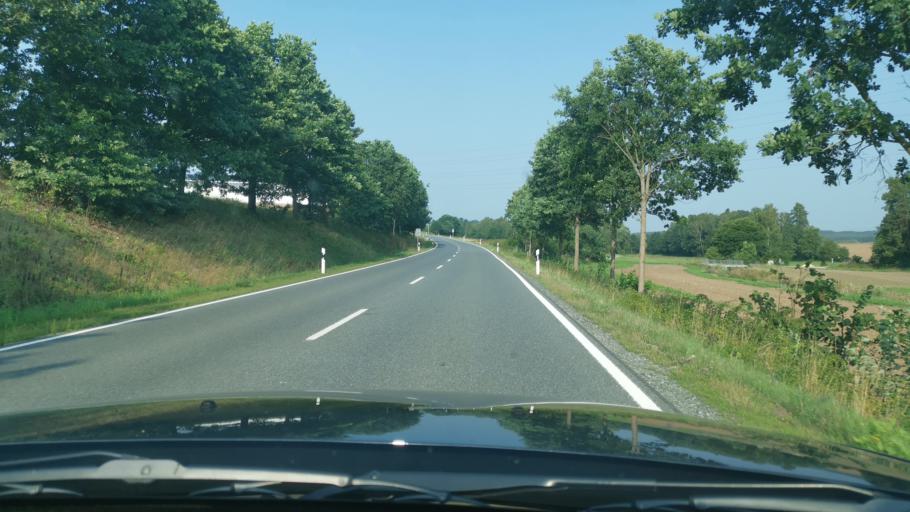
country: DE
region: Bavaria
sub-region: Upper Palatinate
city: Schnaittenbach
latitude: 49.5511
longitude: 12.0292
